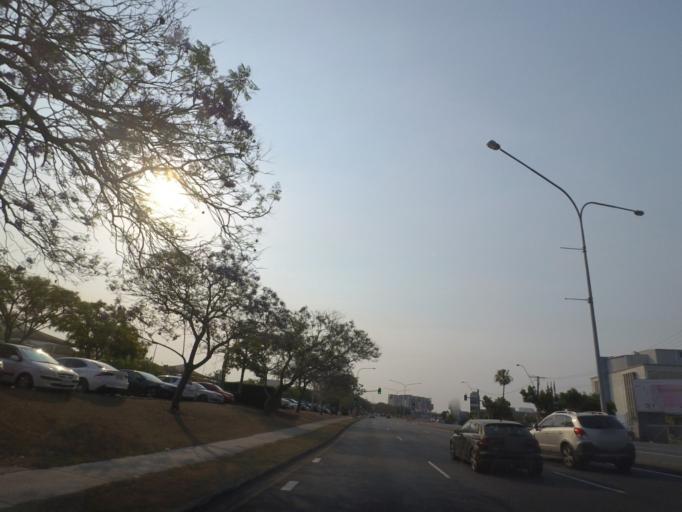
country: AU
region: Queensland
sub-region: Brisbane
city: Upper Mount Gravatt
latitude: -27.5623
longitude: 153.0845
